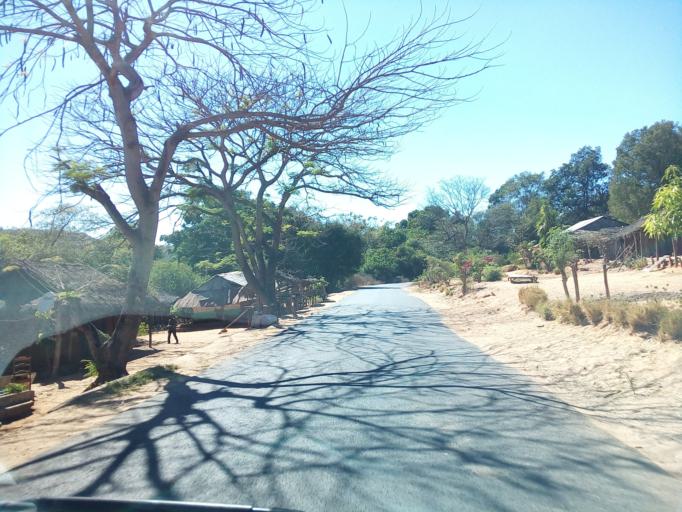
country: MG
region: Boeny
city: Ambato Boeny
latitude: -16.3215
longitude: 46.8277
